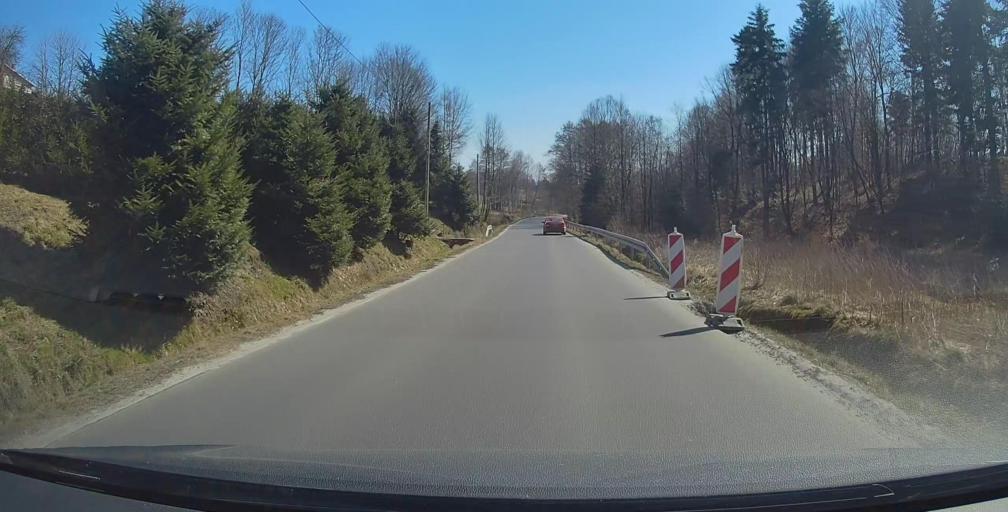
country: PL
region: Subcarpathian Voivodeship
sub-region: Powiat rzeszowski
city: Hyzne
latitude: 49.8918
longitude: 22.2246
